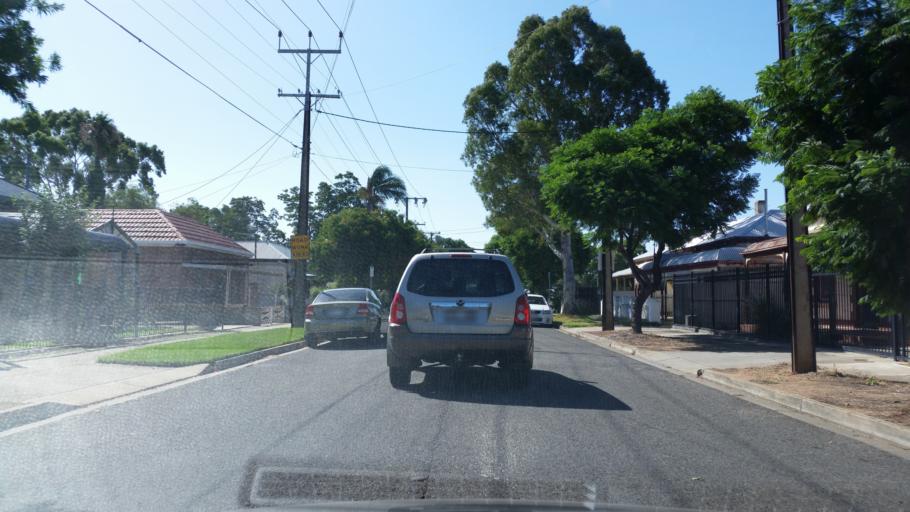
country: AU
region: South Australia
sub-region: Charles Sturt
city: Allenby Gardens
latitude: -34.9018
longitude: 138.5640
